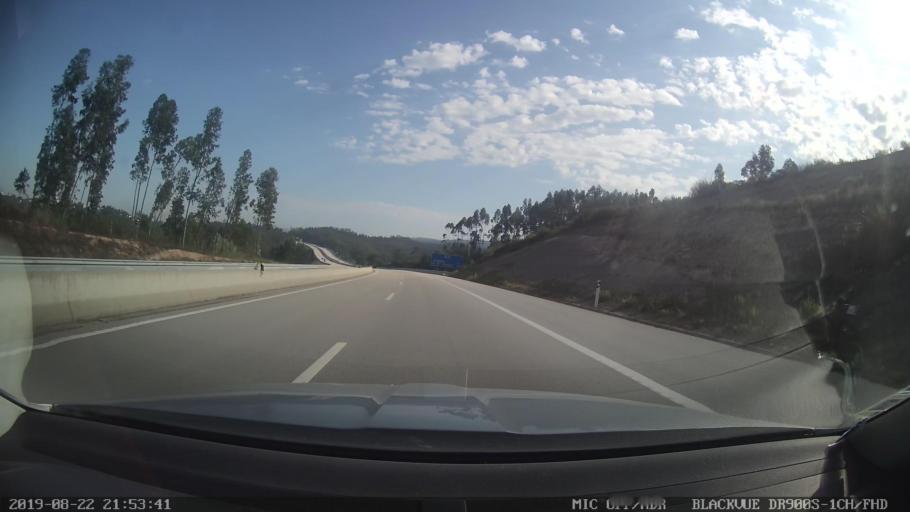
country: PT
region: Coimbra
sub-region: Miranda do Corvo
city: Miranda do Corvo
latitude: 40.1207
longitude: -8.3842
